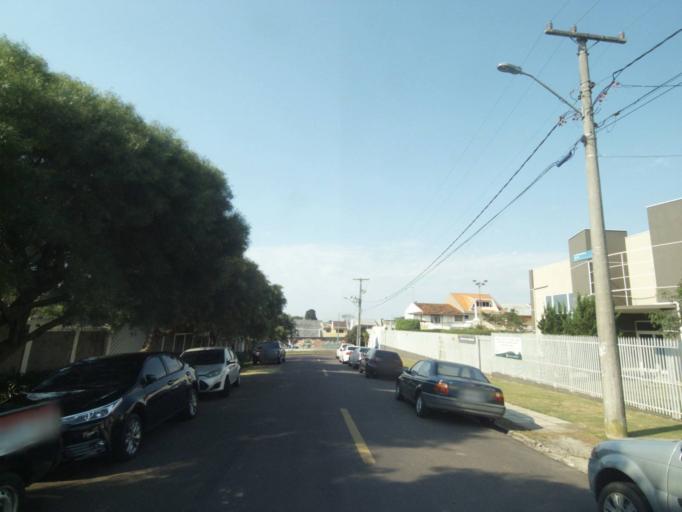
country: BR
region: Parana
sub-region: Sao Jose Dos Pinhais
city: Sao Jose dos Pinhais
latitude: -25.5109
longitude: -49.2604
